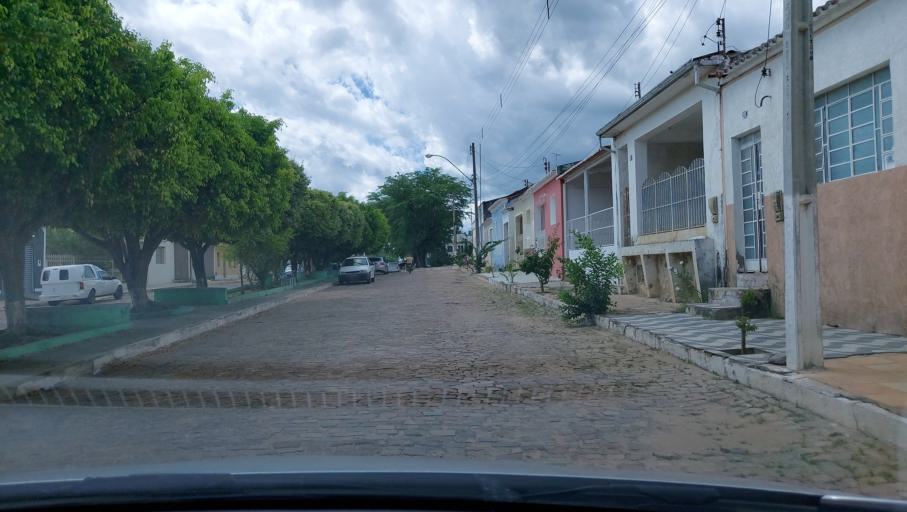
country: BR
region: Bahia
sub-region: Oliveira Dos Brejinhos
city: Beira Rio
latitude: -12.0001
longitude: -42.6261
